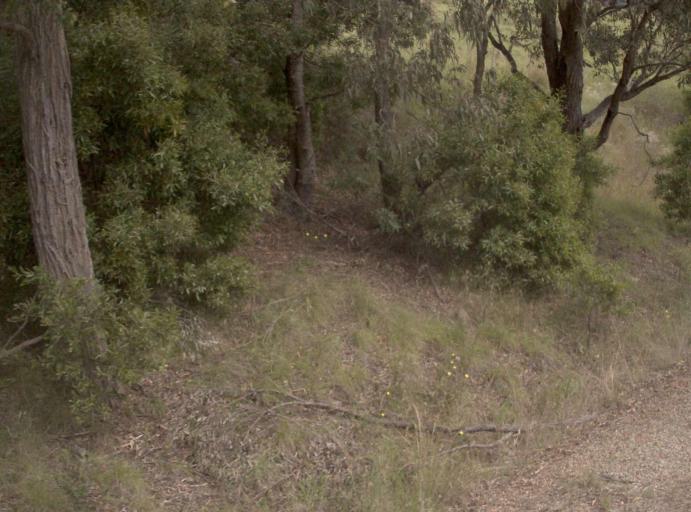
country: AU
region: Victoria
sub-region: East Gippsland
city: Bairnsdale
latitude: -37.5844
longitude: 147.1833
